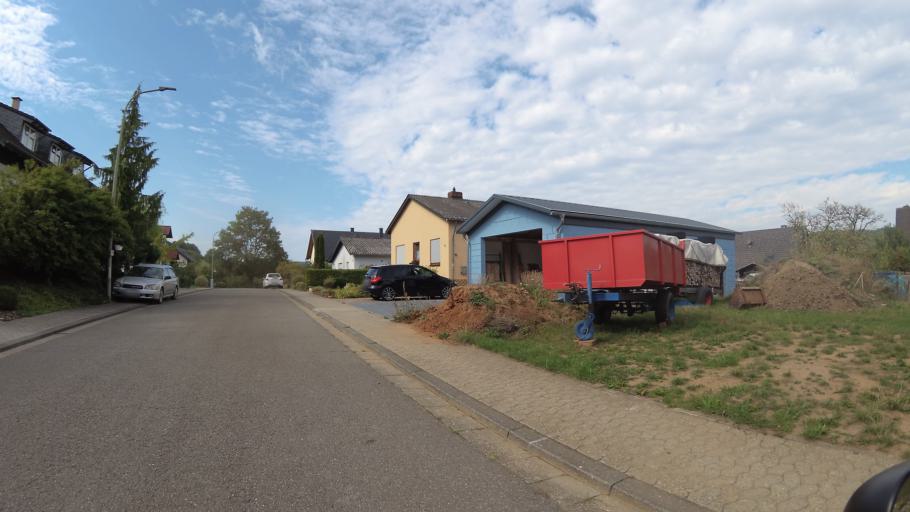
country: DE
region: Saarland
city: Gersheim
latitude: 49.1707
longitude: 7.2356
